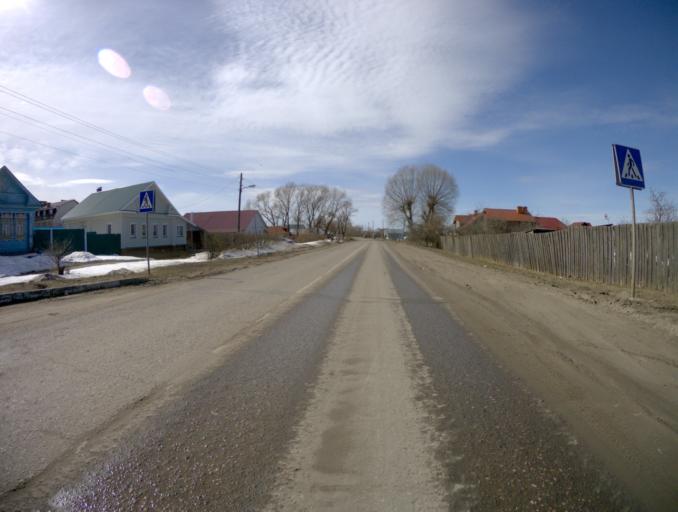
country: RU
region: Vladimir
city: Suzdal'
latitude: 56.4264
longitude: 40.4281
